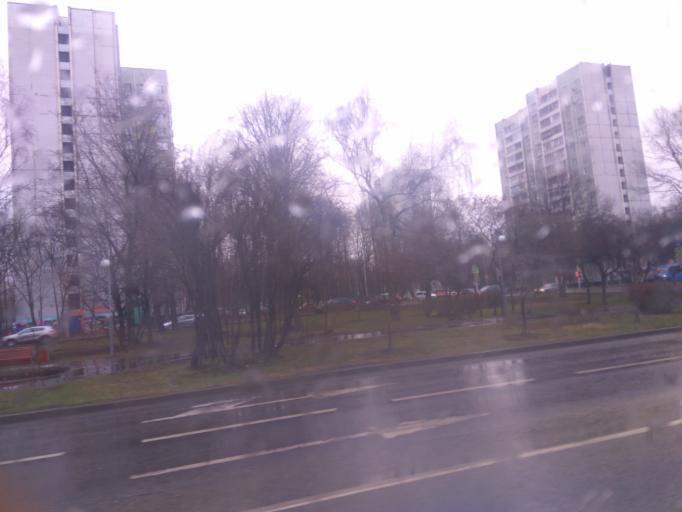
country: RU
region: Moscow
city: Lianozovo
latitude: 55.8982
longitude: 37.5791
